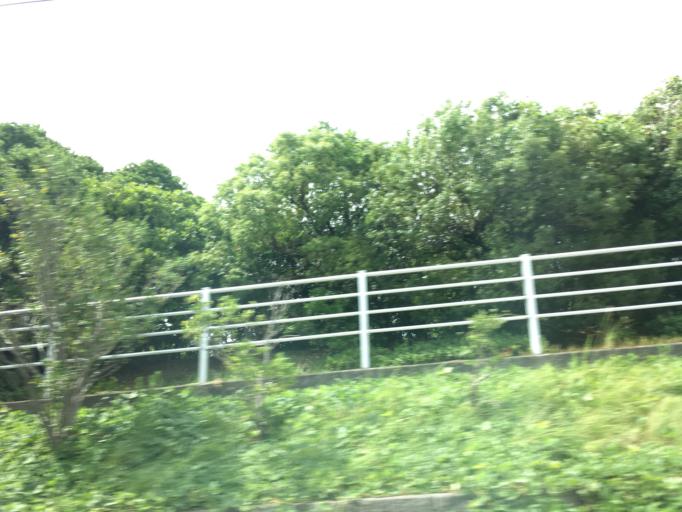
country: JP
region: Hyogo
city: Nishinomiya-hama
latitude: 34.7198
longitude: 135.3233
